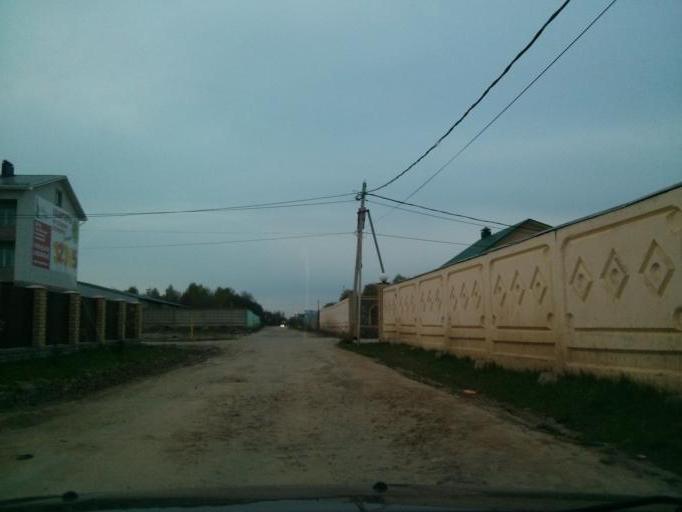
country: RU
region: Vladimir
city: Murom
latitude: 55.5455
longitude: 42.0651
